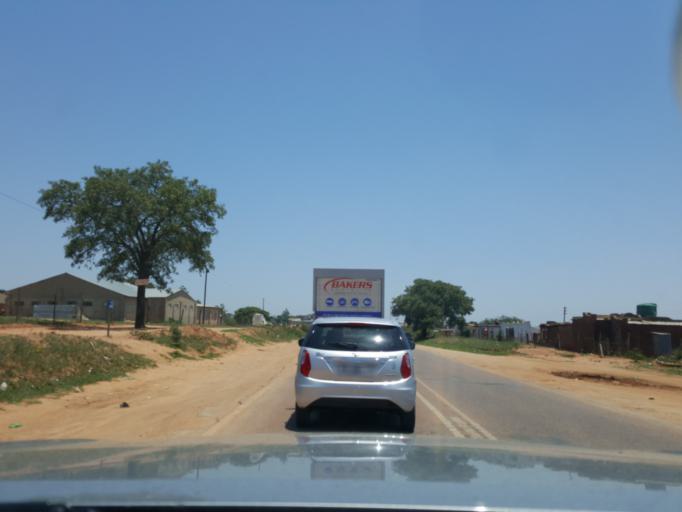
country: ZA
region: Limpopo
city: Thulamahashi
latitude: -24.6186
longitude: 31.0393
